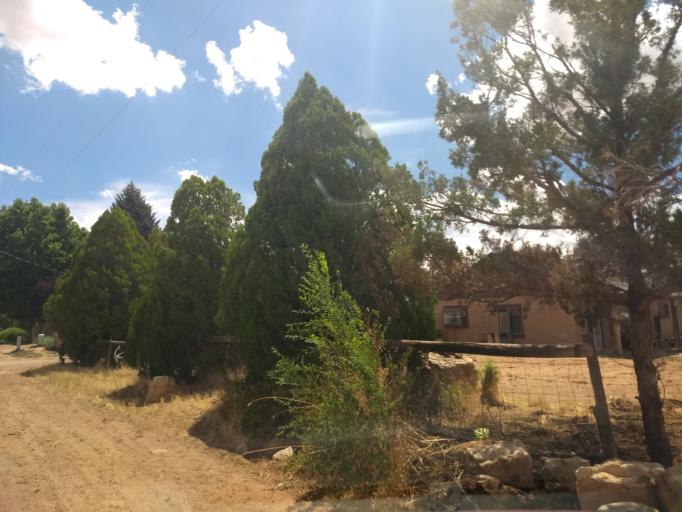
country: US
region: Arizona
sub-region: Coconino County
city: Fredonia
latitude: 36.9473
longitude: -112.5320
